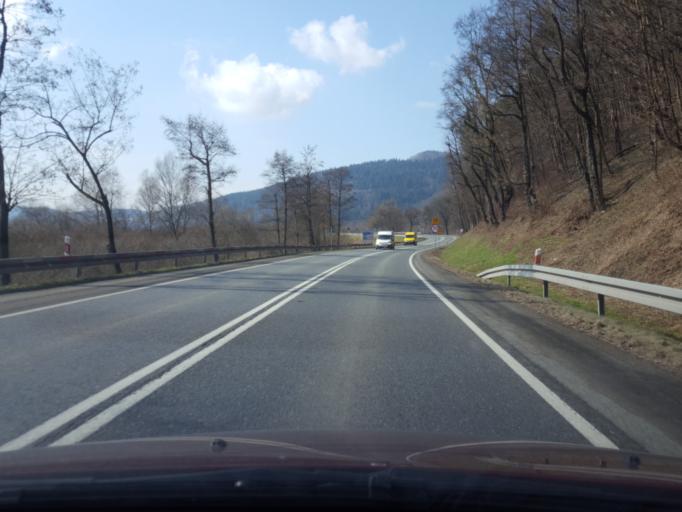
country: PL
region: Lesser Poland Voivodeship
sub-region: Powiat nowosadecki
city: Lososina Dolna
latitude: 49.6936
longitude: 20.6573
